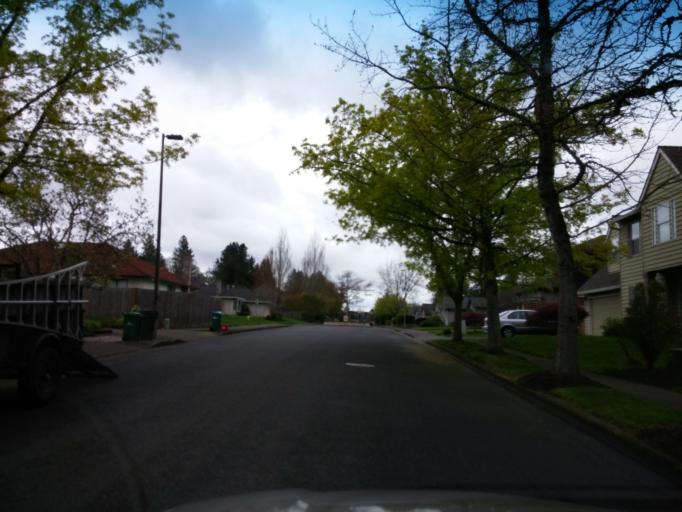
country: US
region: Oregon
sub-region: Washington County
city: Oak Hills
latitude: 45.5156
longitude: -122.8484
